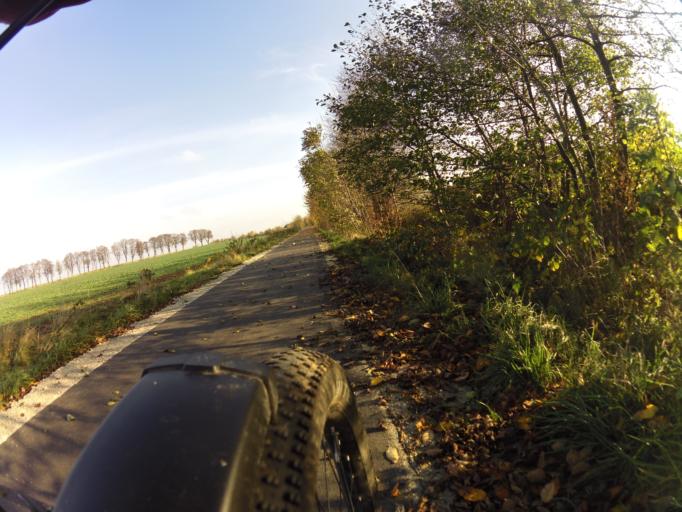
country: PL
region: Pomeranian Voivodeship
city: Strzelno
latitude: 54.7653
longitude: 18.2754
